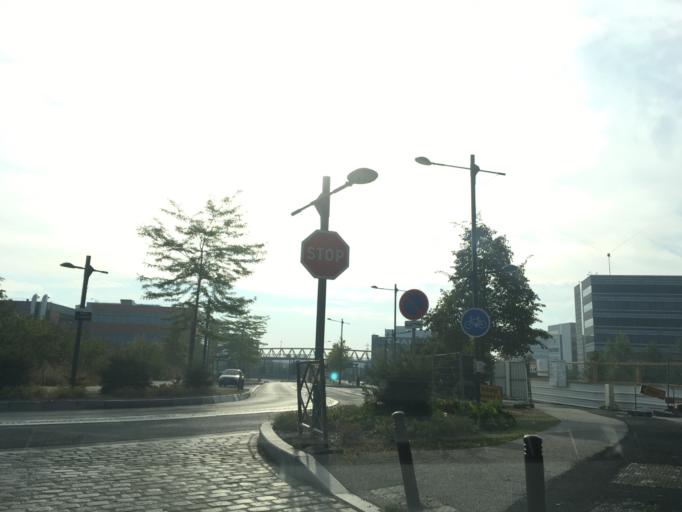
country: FR
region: Ile-de-France
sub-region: Departement des Hauts-de-Seine
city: Gennevilliers
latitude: 48.9411
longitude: 2.3051
